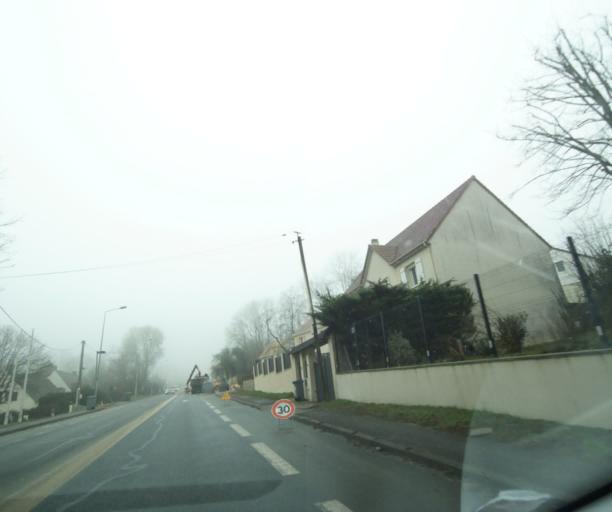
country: FR
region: Ile-de-France
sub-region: Departement de Seine-et-Marne
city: Dammartin-en-Goele
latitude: 49.0556
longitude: 2.6959
